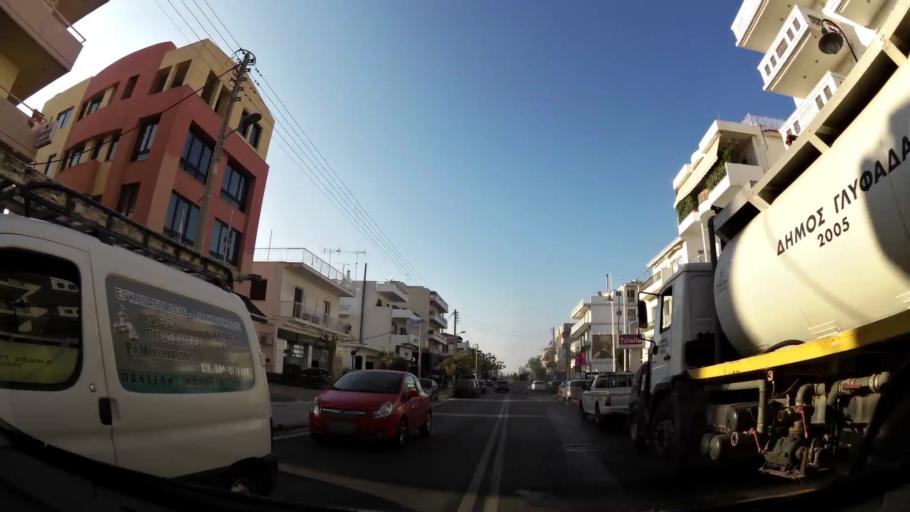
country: GR
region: Attica
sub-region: Nomarchia Athinas
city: Argyroupoli
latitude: 37.8922
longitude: 23.7651
